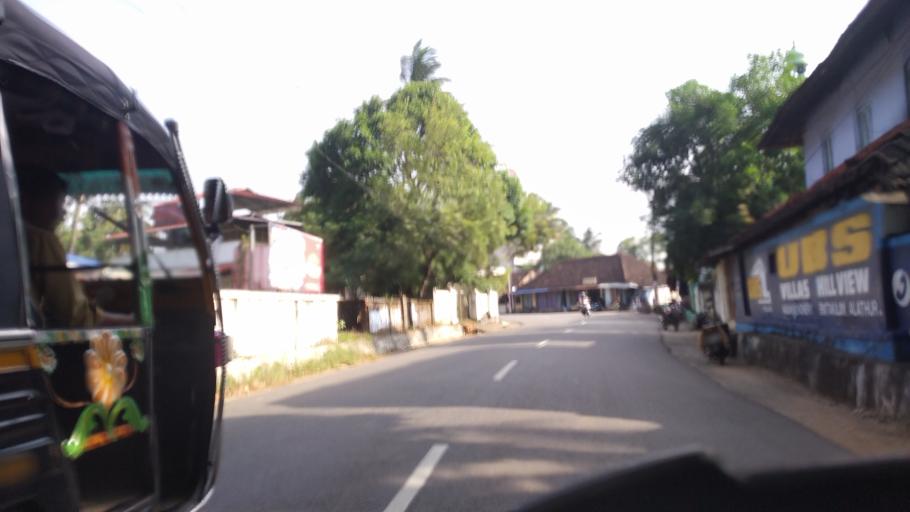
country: IN
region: Kerala
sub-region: Palakkad district
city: Palakkad
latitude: 10.6000
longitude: 76.5505
